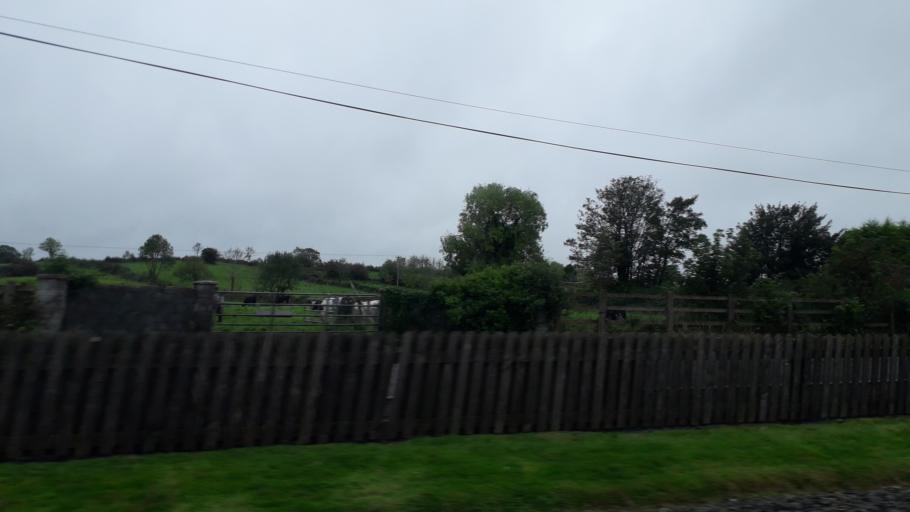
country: IE
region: Connaught
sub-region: Roscommon
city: Ballaghaderreen
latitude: 53.8869
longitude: -8.4757
